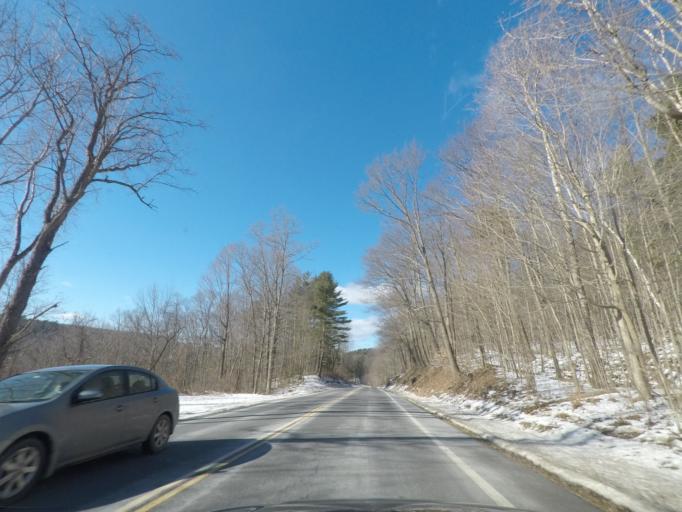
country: US
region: Massachusetts
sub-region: Berkshire County
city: Richmond
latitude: 42.3959
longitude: -73.4146
